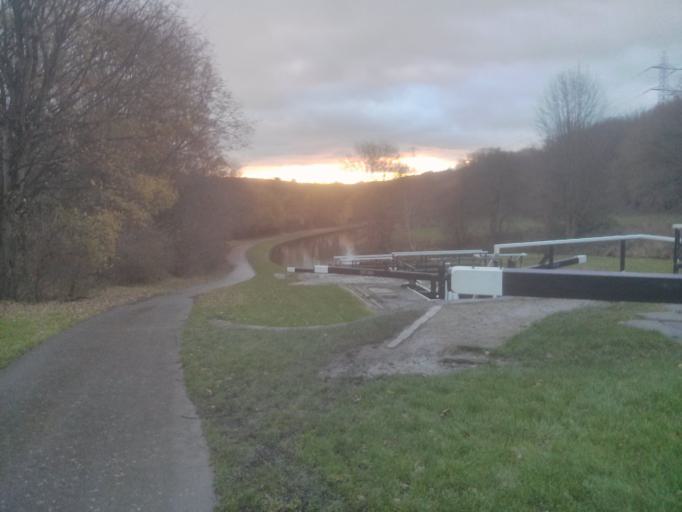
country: GB
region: England
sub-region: City and Borough of Leeds
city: Horsforth
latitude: 53.8261
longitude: -1.6335
